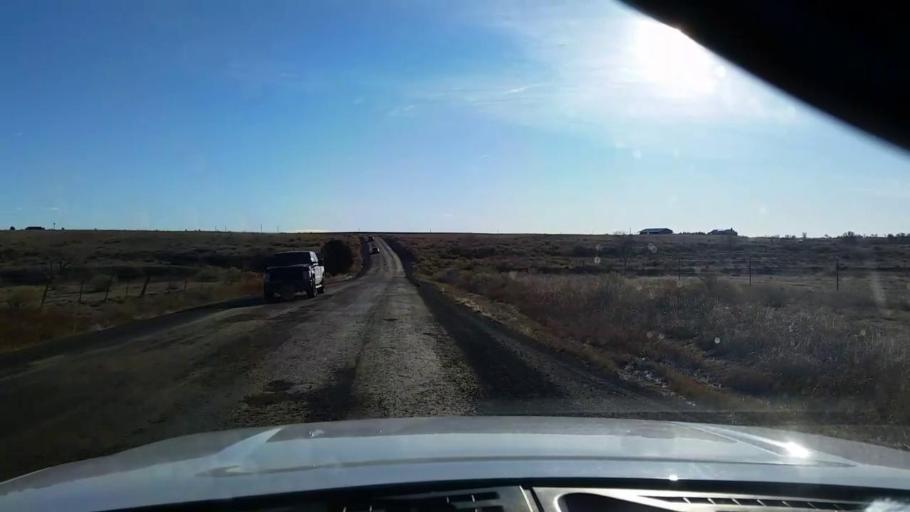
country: US
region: Colorado
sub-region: Larimer County
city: Wellington
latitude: 40.7708
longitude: -105.1191
